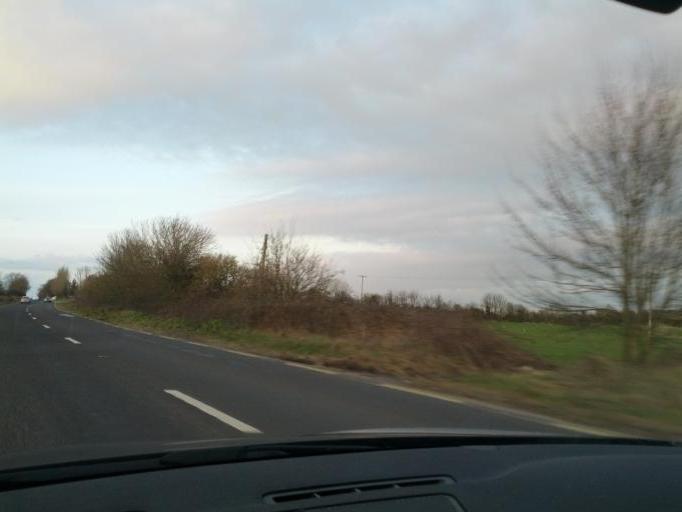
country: IE
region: Munster
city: Nenagh Bridge
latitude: 52.9044
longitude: -8.1841
